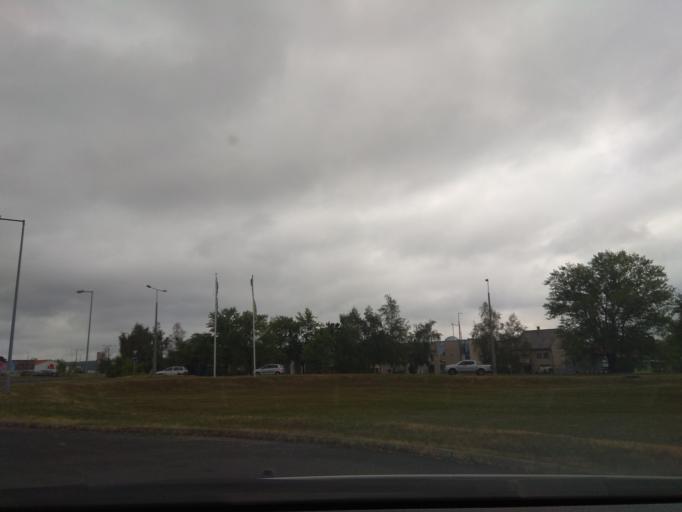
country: HU
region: Borsod-Abauj-Zemplen
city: Miskolc
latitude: 48.0573
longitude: 20.7983
